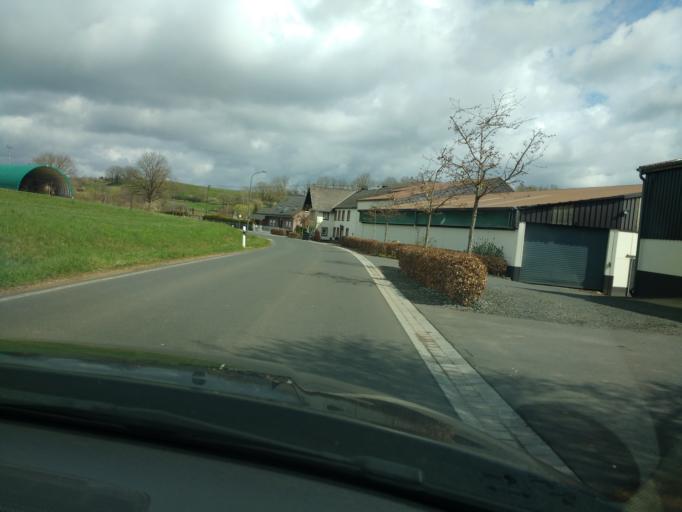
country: DE
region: Rheinland-Pfalz
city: Duppach
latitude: 50.2573
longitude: 6.5704
